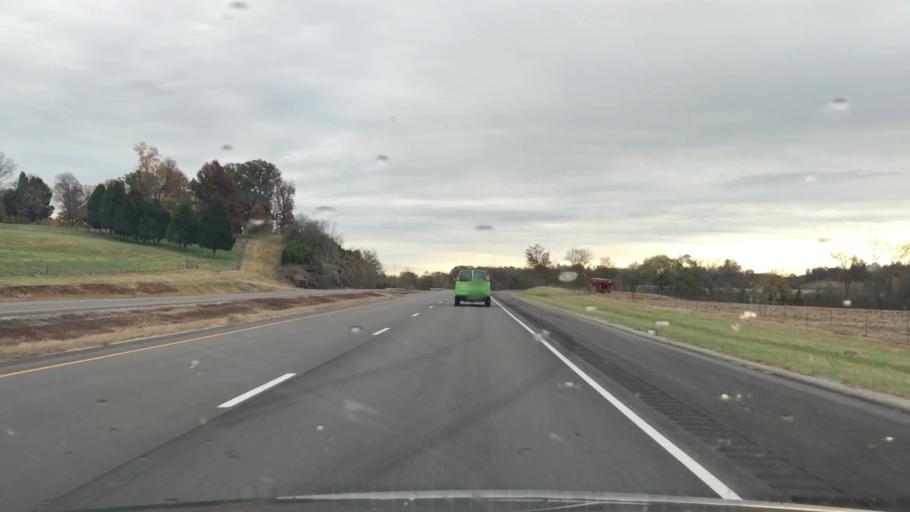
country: US
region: Kentucky
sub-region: Barren County
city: Glasgow
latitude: 37.0342
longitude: -85.9133
